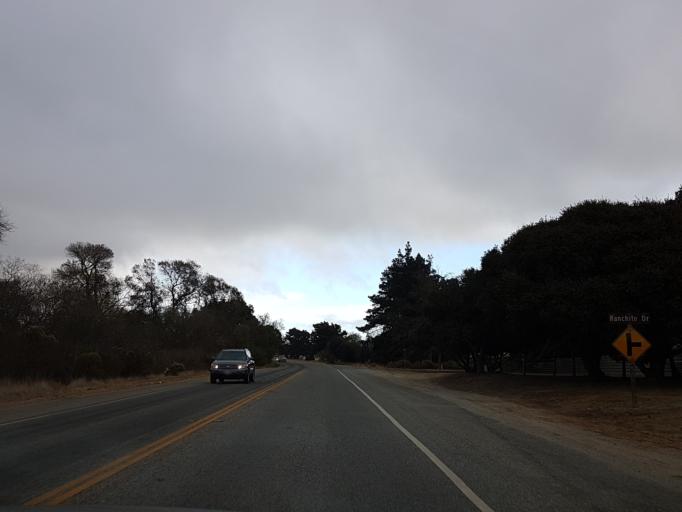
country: US
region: California
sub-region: Monterey County
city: Salinas
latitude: 36.6043
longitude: -121.6383
